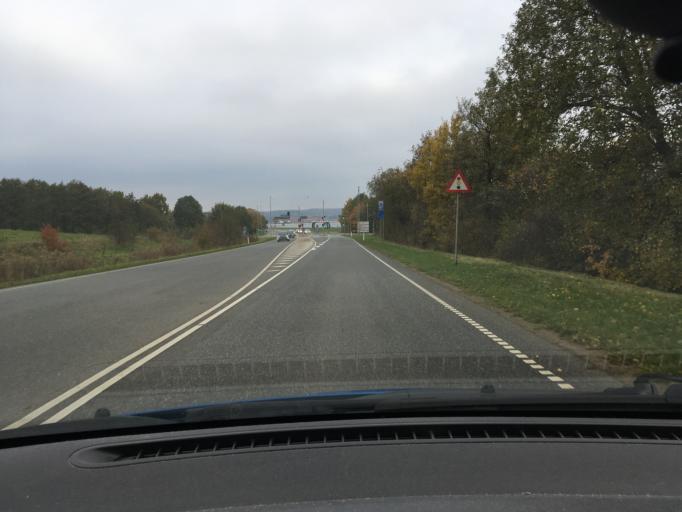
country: DK
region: South Denmark
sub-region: Aabenraa Kommune
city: Aabenraa
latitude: 55.0211
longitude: 9.4261
